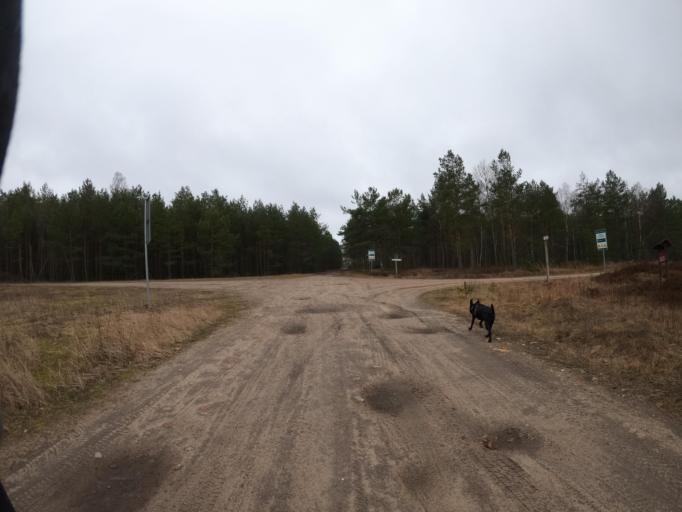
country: PL
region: Greater Poland Voivodeship
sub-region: Powiat zlotowski
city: Sypniewo
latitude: 53.5150
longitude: 16.5630
